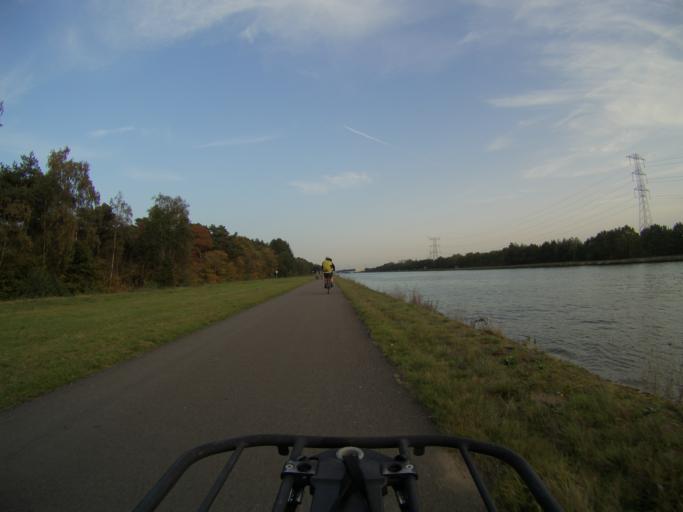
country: BE
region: Flanders
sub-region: Provincie Antwerpen
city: Nijlen
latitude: 51.1888
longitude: 4.6792
